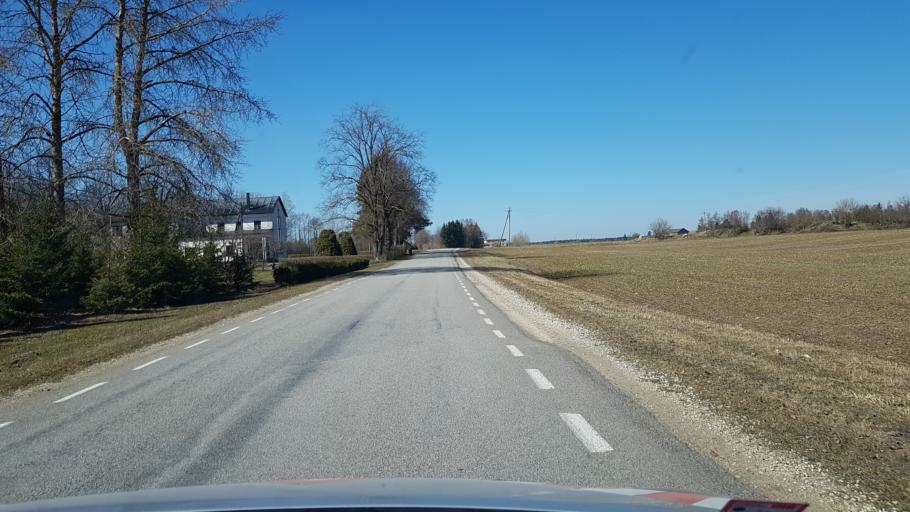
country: EE
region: Laeaene-Virumaa
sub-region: Vaeike-Maarja vald
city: Vaike-Maarja
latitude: 59.1087
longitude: 26.3782
